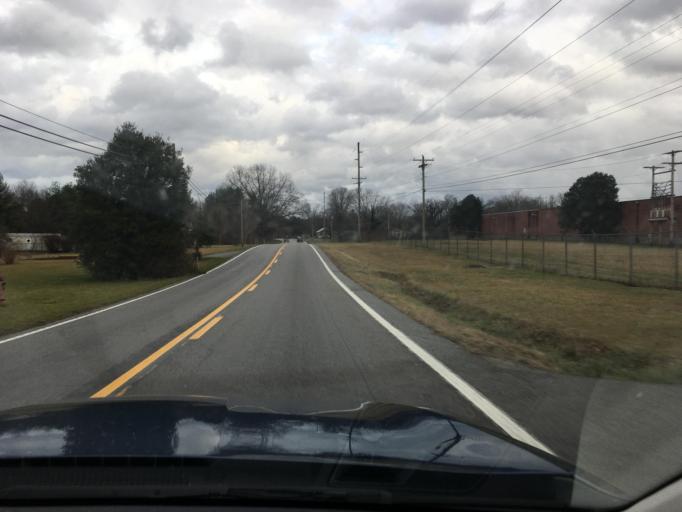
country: US
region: Tennessee
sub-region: Cumberland County
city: Crossville
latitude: 35.9053
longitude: -84.9793
